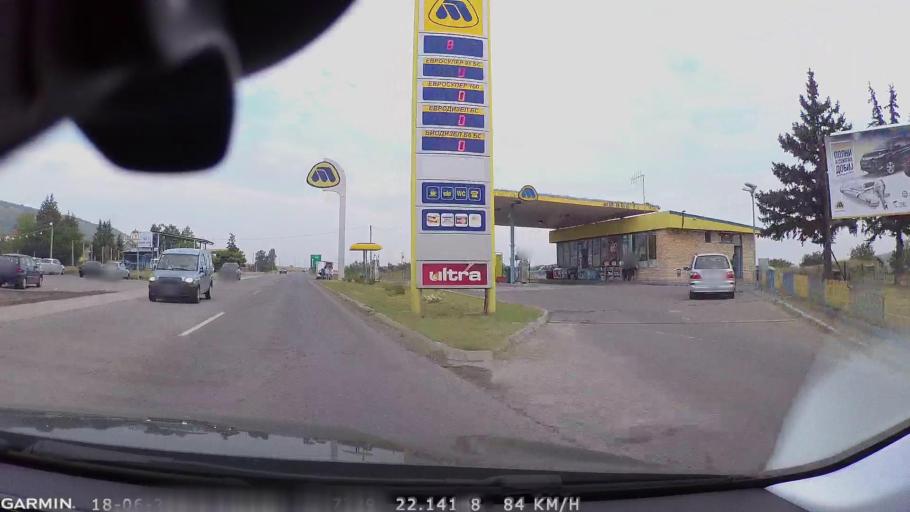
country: MK
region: Stip
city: Shtip
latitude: 41.7735
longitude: 22.1401
